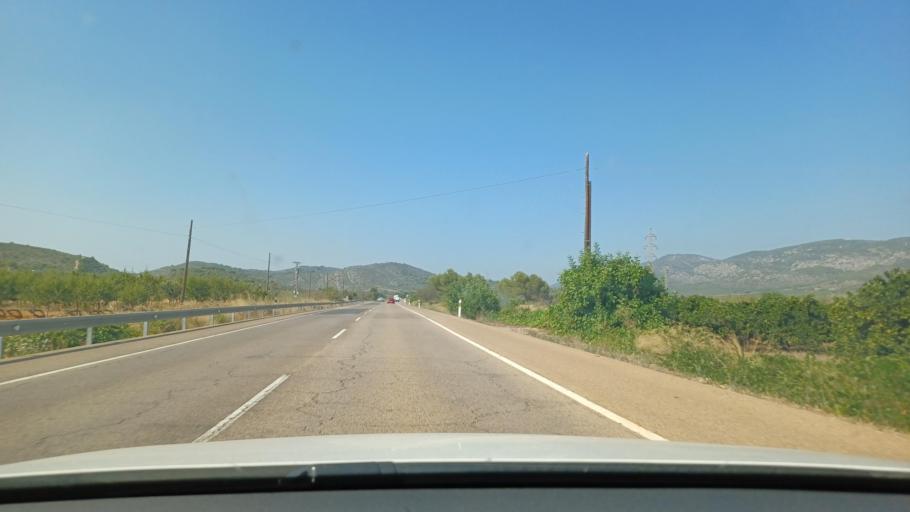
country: ES
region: Valencia
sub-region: Provincia de Castello
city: Alcala de Xivert
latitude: 40.2565
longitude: 0.2366
